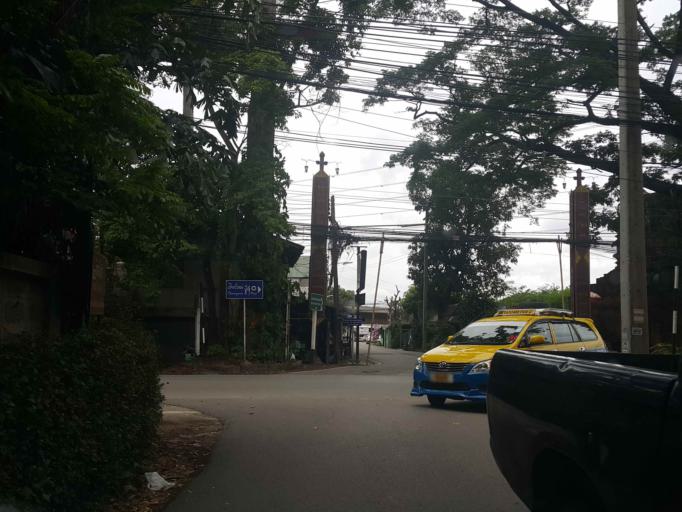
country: TH
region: Chiang Mai
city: Saraphi
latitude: 18.7493
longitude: 99.0107
